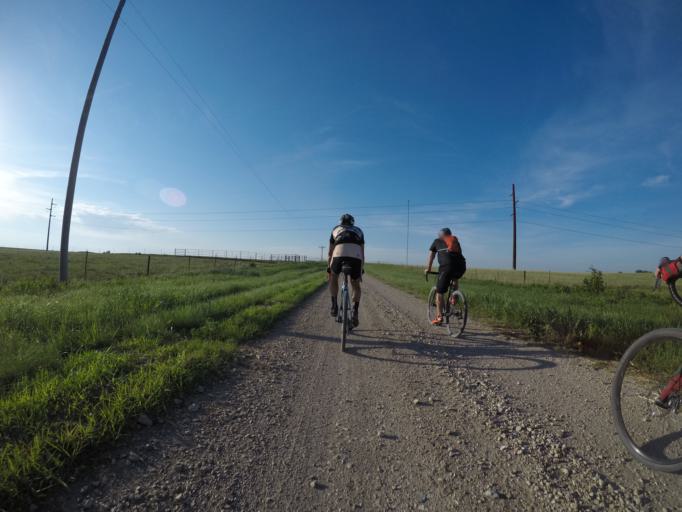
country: US
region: Kansas
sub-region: Riley County
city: Manhattan
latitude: 38.9968
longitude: -96.4921
